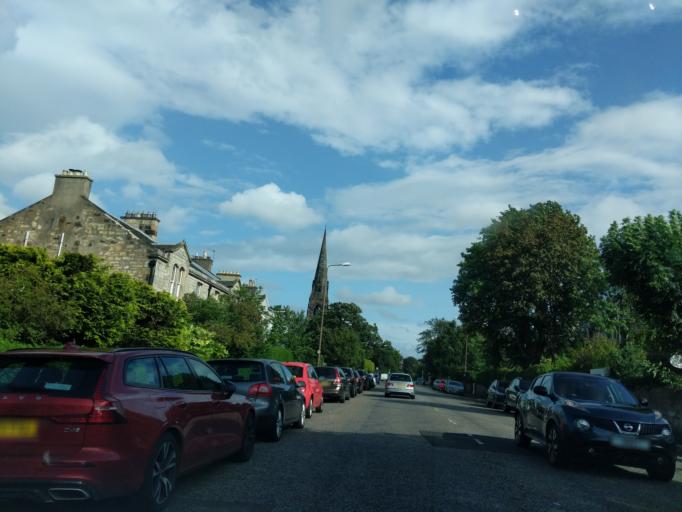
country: GB
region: Scotland
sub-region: West Lothian
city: Seafield
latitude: 55.9506
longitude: -3.1055
